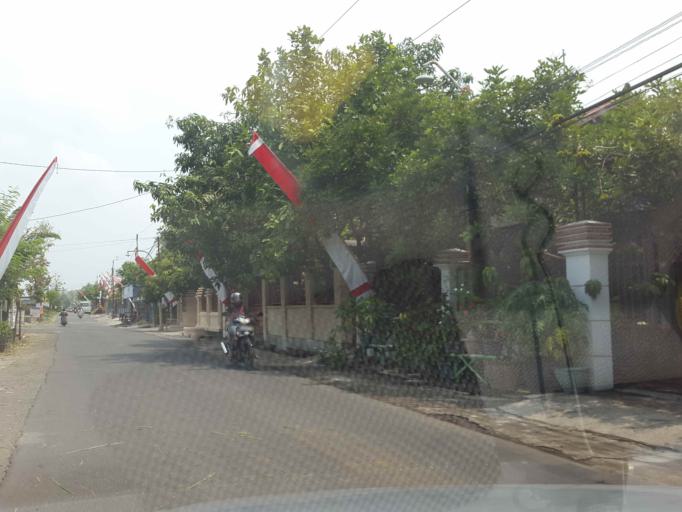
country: ID
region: Central Java
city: Jaten
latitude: -7.5865
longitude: 110.9423
